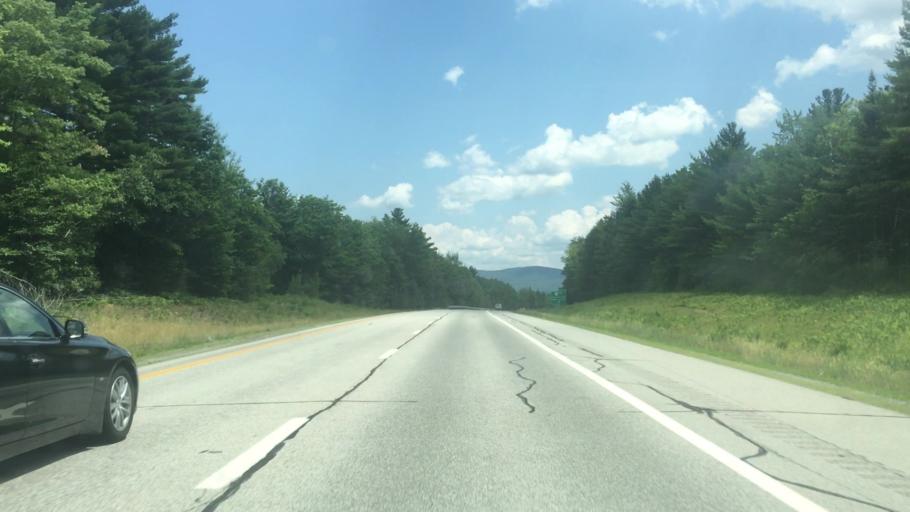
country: US
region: New Hampshire
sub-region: Merrimack County
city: New London
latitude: 43.3940
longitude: -71.9925
